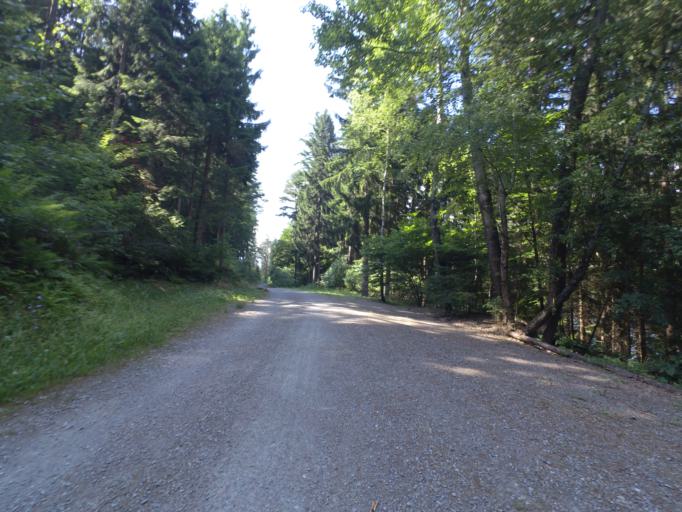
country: AT
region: Carinthia
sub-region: Politischer Bezirk Spittal an der Drau
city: Millstatt
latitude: 46.7829
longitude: 13.5931
